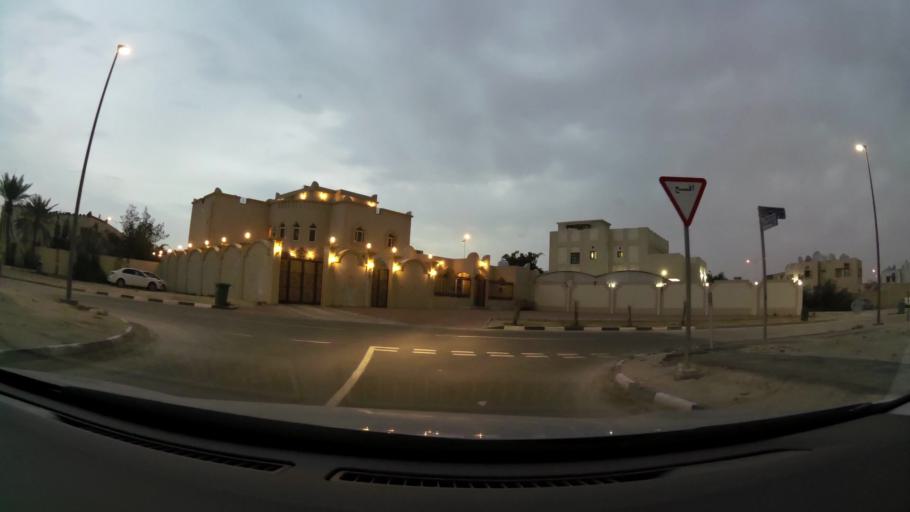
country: QA
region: Baladiyat ad Dawhah
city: Doha
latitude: 25.3417
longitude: 51.5117
